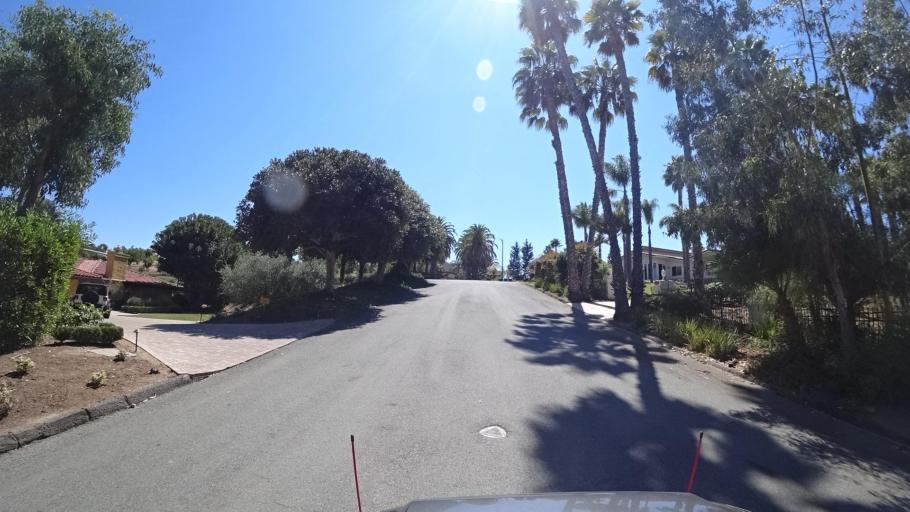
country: US
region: California
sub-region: San Diego County
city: Rancho Santa Fe
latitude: 33.0281
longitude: -117.1708
